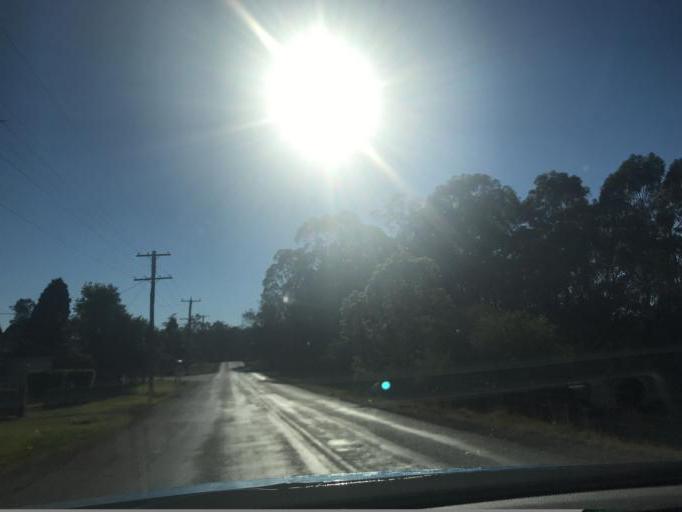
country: AU
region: New South Wales
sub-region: Cessnock
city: Cessnock
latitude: -32.9057
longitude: 151.2867
